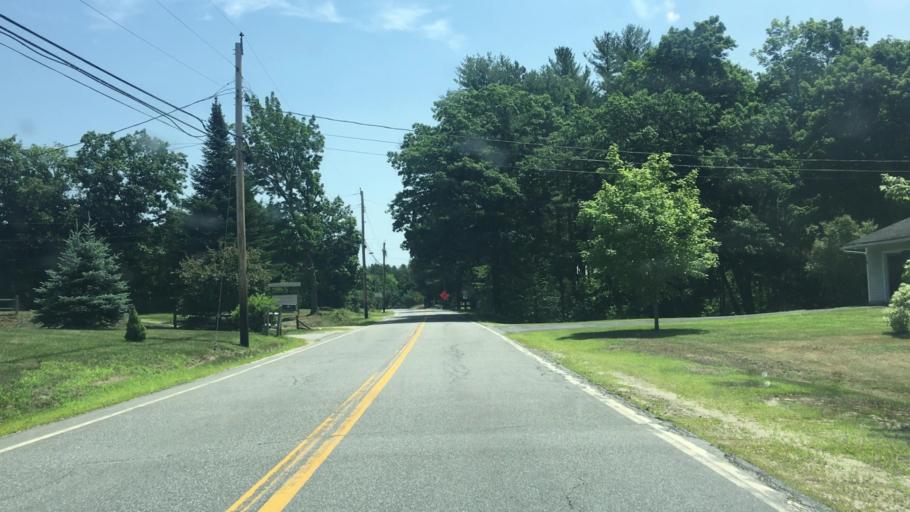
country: US
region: Maine
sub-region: Androscoggin County
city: Livermore
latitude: 44.3855
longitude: -70.2525
